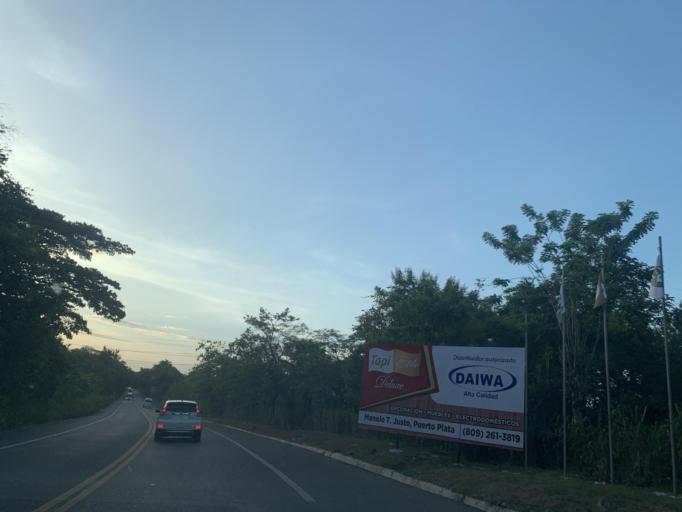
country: DO
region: Puerto Plata
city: Imbert
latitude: 19.7640
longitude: -70.8332
